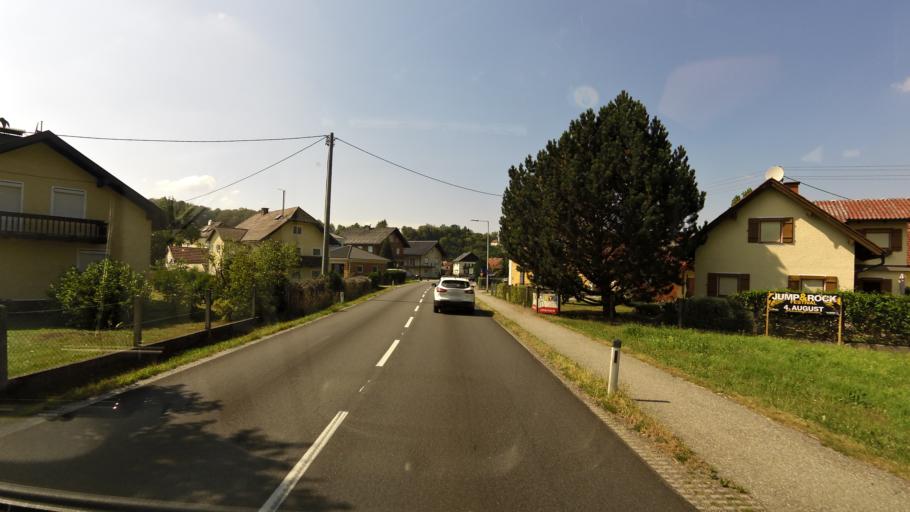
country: AT
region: Upper Austria
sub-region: Politischer Bezirk Braunau am Inn
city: Braunau am Inn
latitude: 48.1505
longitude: 13.1225
